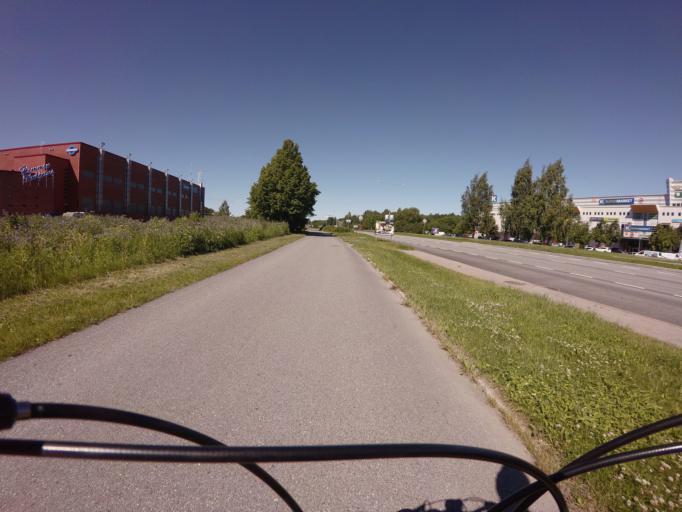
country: FI
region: Varsinais-Suomi
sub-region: Turku
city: Turku
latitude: 60.4564
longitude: 22.2349
